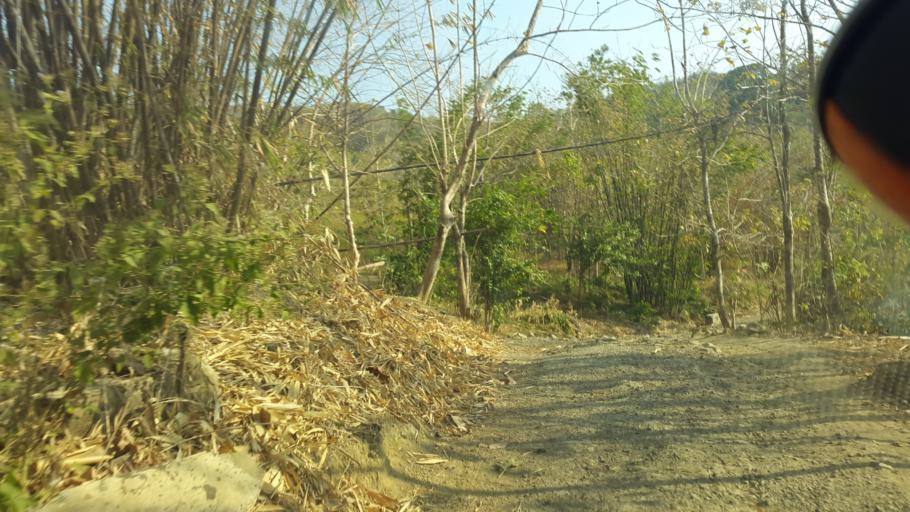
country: ID
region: West Java
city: Sindangasih
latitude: -7.2514
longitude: 106.4731
